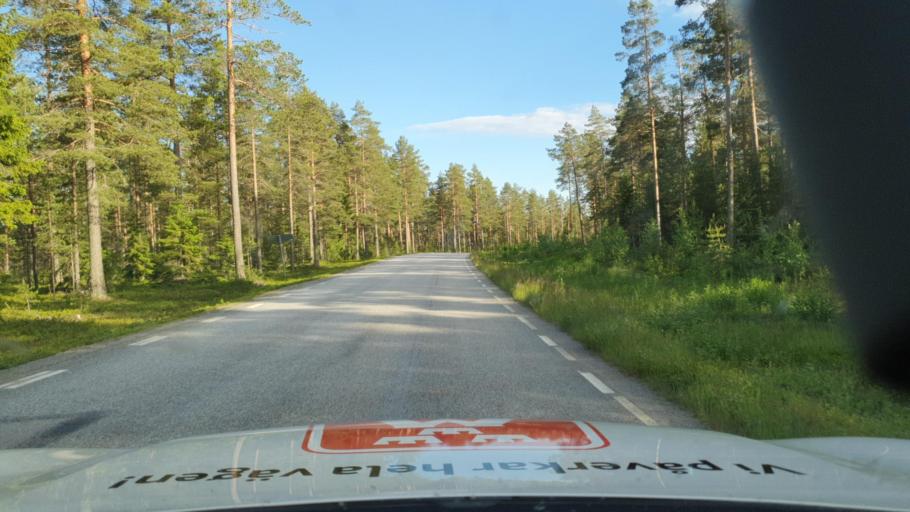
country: SE
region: Vaesterbotten
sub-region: Umea Kommun
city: Roback
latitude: 63.8972
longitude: 20.1574
